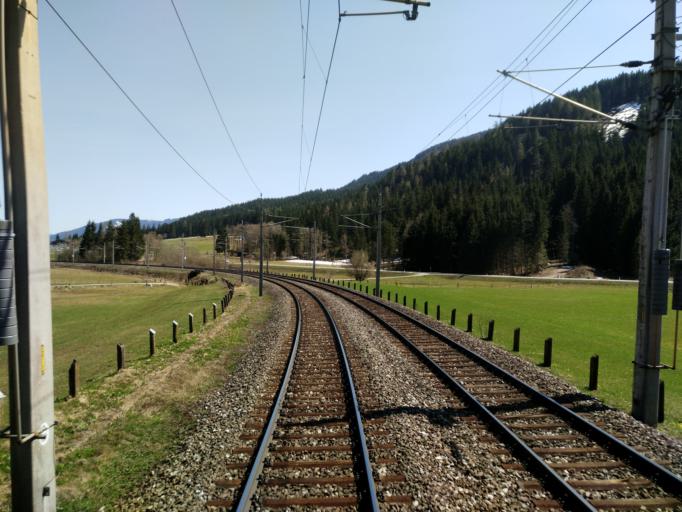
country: AT
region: Tyrol
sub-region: Politischer Bezirk Kitzbuhel
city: Hochfilzen
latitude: 47.4546
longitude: 12.6577
